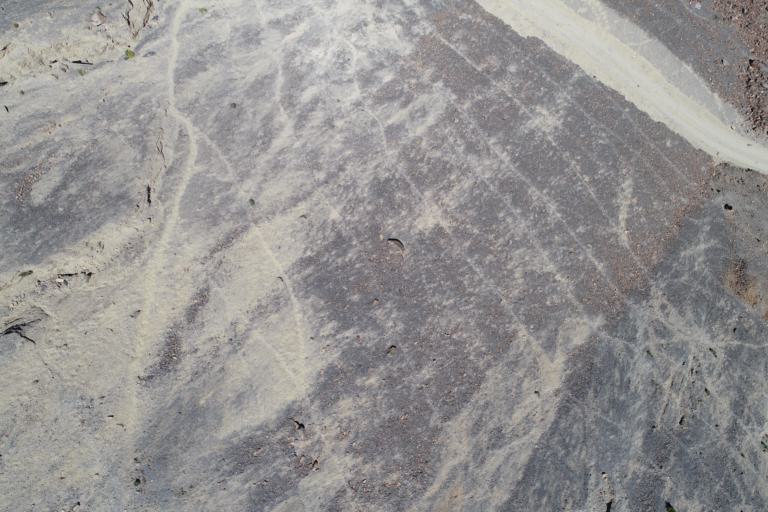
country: BO
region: La Paz
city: La Paz
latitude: -16.6215
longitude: -67.8251
